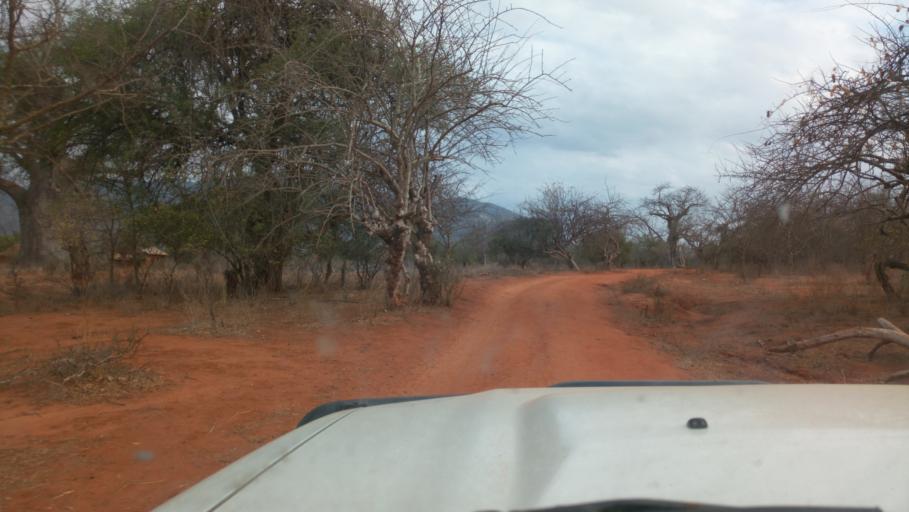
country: KE
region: Kitui
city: Kitui
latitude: -1.7270
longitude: 38.3838
